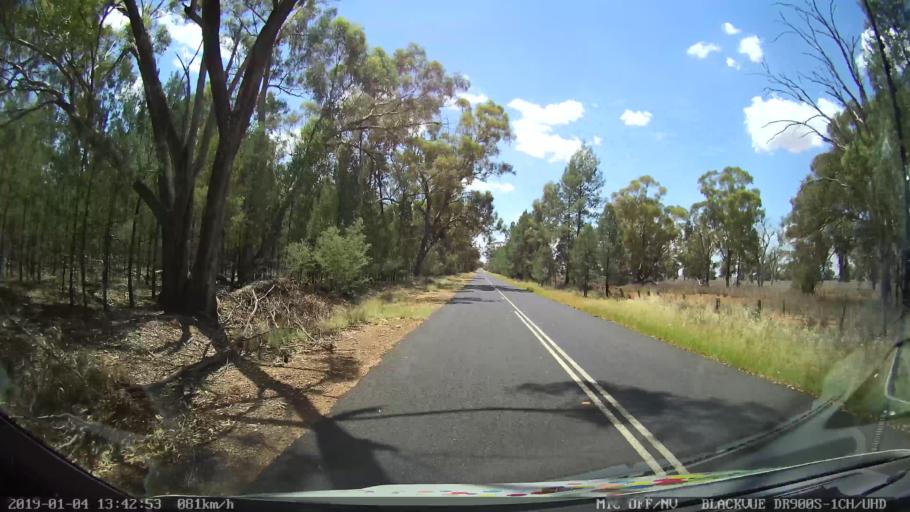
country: AU
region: New South Wales
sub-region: Dubbo Municipality
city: Dubbo
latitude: -32.4847
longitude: 148.5574
